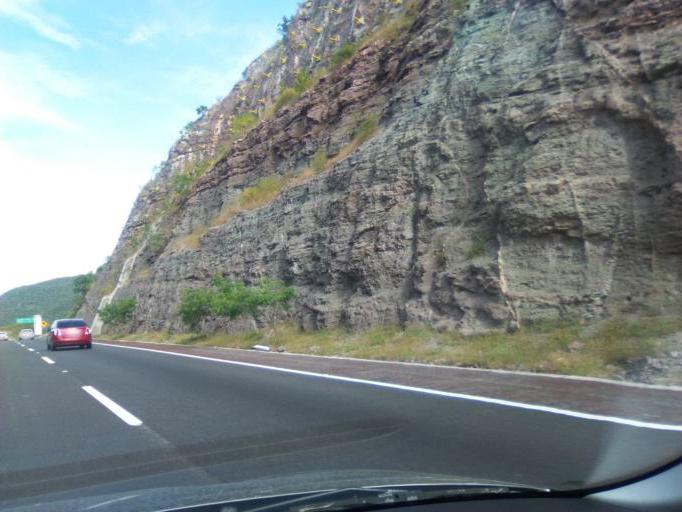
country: MX
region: Guerrero
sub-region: Huitzuco de los Figueroa
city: San Francisco Ozomatlan
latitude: 17.9535
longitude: -99.3538
